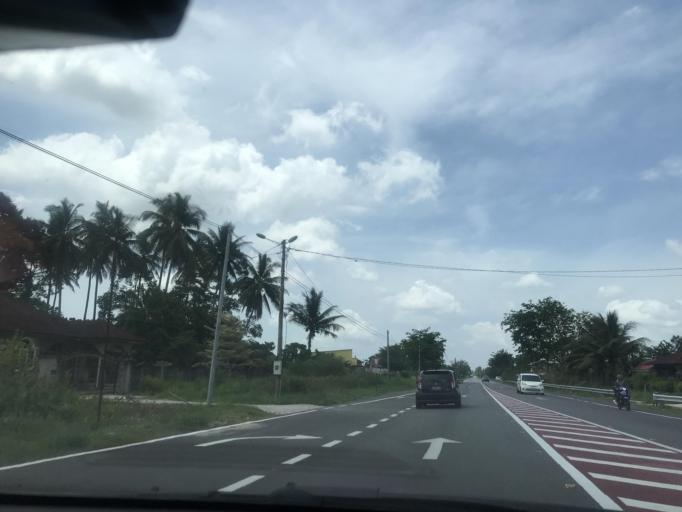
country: MY
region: Kelantan
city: Kota Bharu
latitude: 6.1518
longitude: 102.2082
